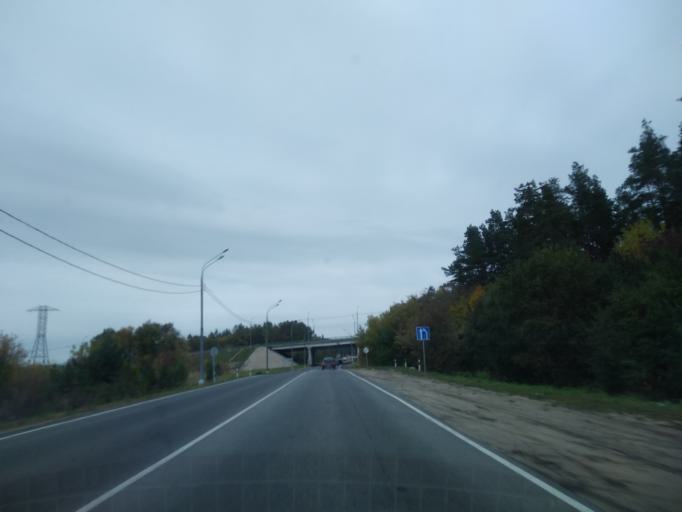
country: RU
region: Lipetsk
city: Zadonsk
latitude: 52.3677
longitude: 38.9173
